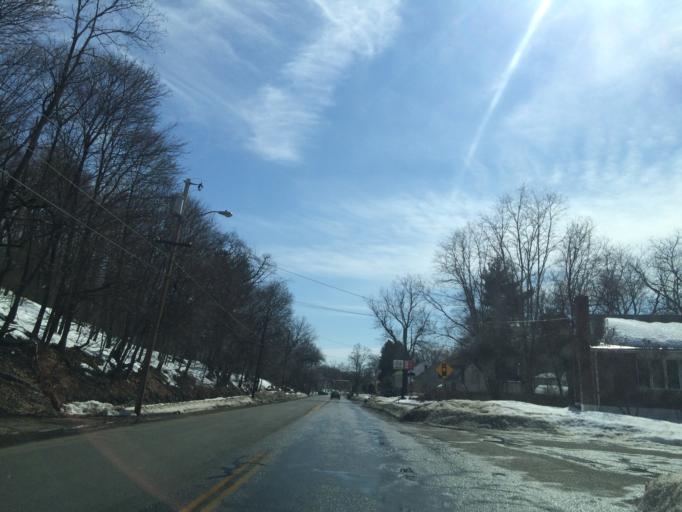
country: US
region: Massachusetts
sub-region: Middlesex County
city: Winchester
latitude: 42.4292
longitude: -71.1290
